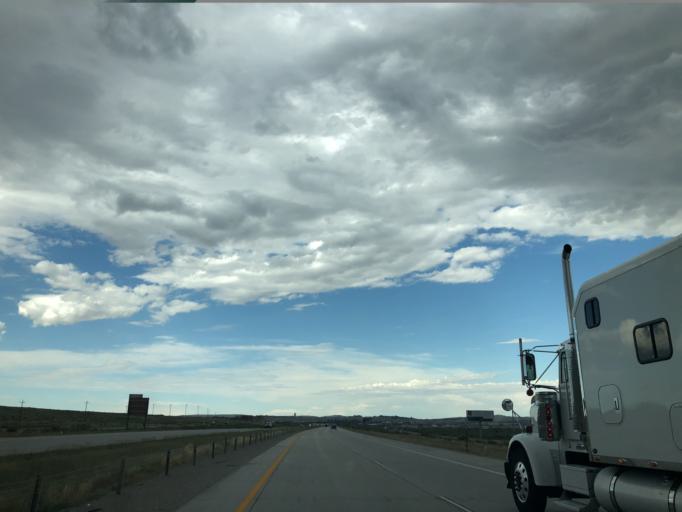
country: US
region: Wyoming
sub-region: Sweetwater County
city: North Rock Springs
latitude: 41.5665
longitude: -109.2894
